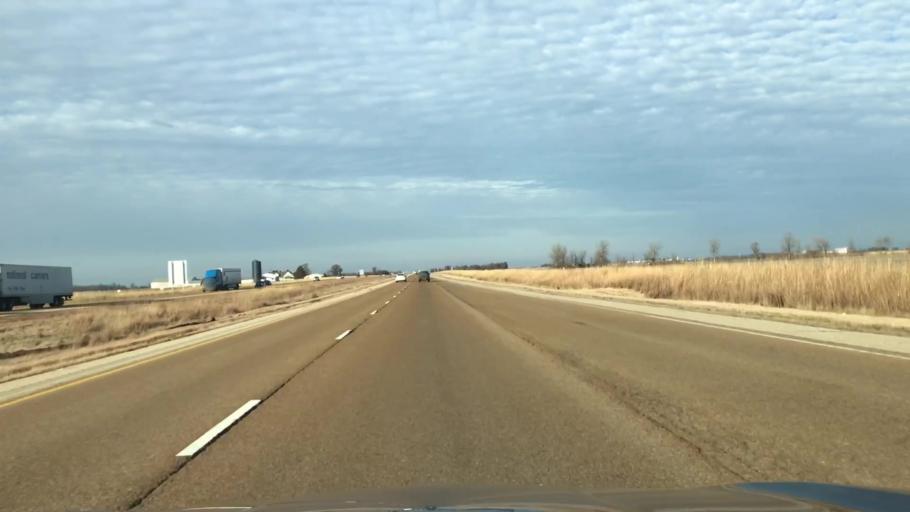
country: US
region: Illinois
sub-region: Montgomery County
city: Raymond
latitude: 39.3264
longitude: -89.6425
